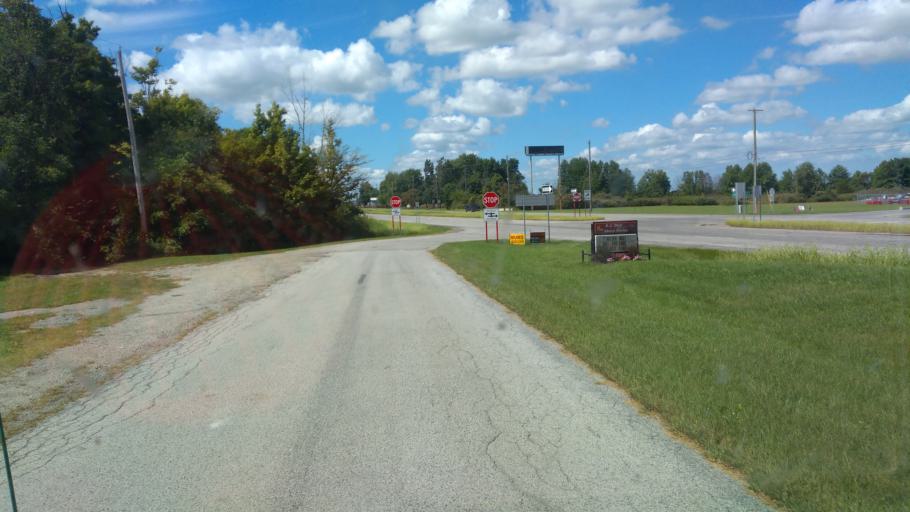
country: US
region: Ohio
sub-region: Huron County
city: Monroeville
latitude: 41.2291
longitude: -82.6566
